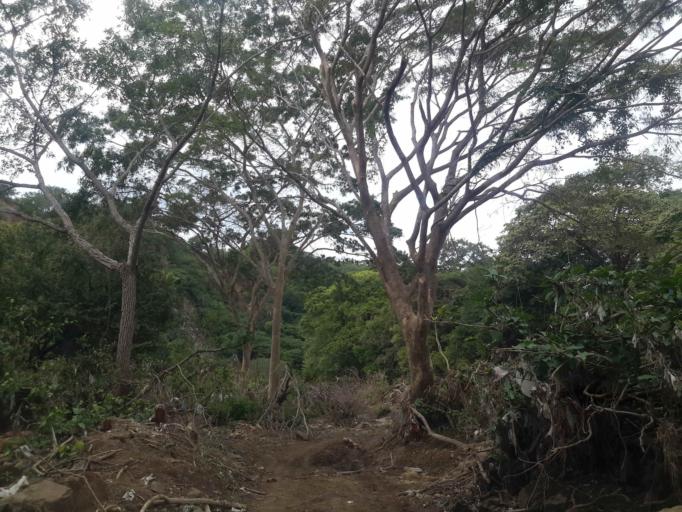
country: NI
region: Carazo
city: Santa Teresa
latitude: 11.6914
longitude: -86.2961
